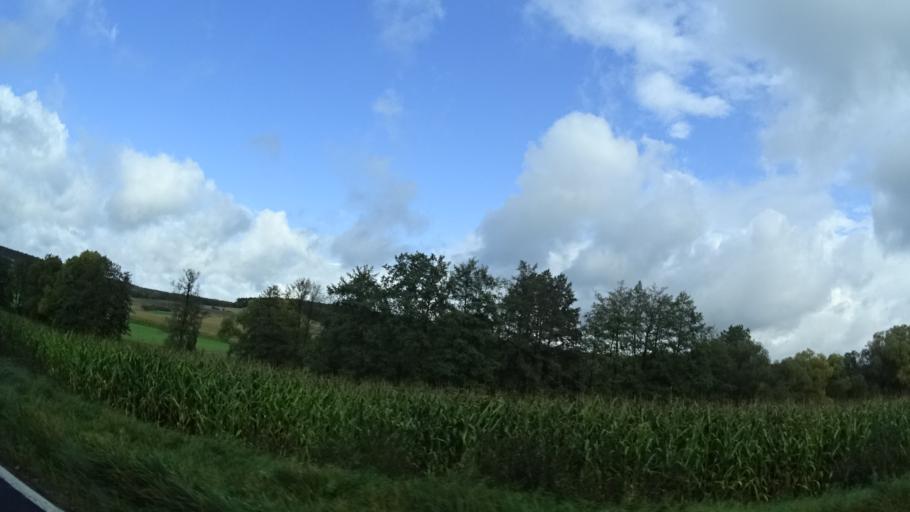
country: DE
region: Bavaria
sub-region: Upper Franconia
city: Burgwindheim
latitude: 49.8762
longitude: 10.6127
